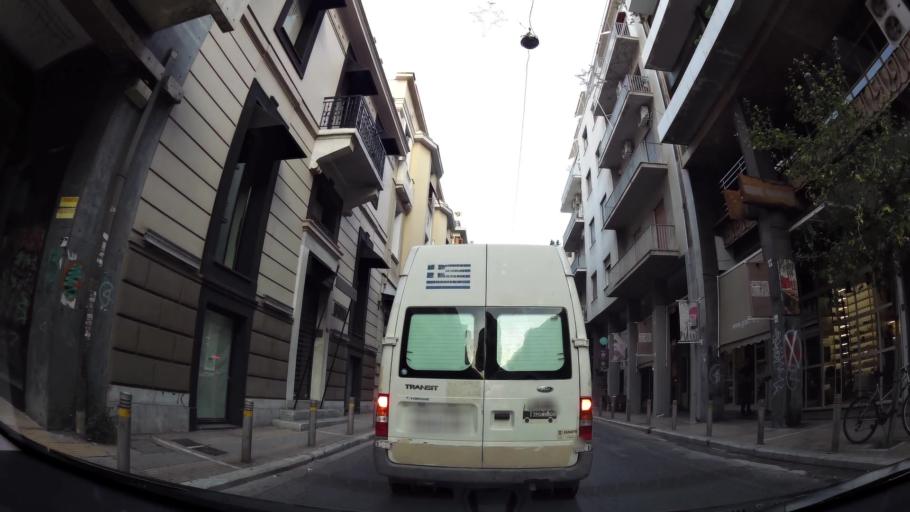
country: GR
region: Attica
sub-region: Nomarchia Athinas
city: Athens
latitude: 37.9789
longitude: 23.7379
